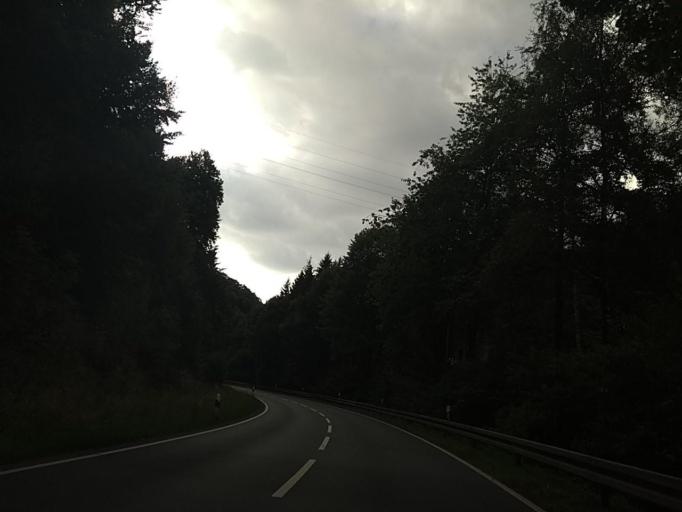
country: DE
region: North Rhine-Westphalia
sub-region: Regierungsbezirk Arnsberg
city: Brilon
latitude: 51.4466
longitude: 8.6346
